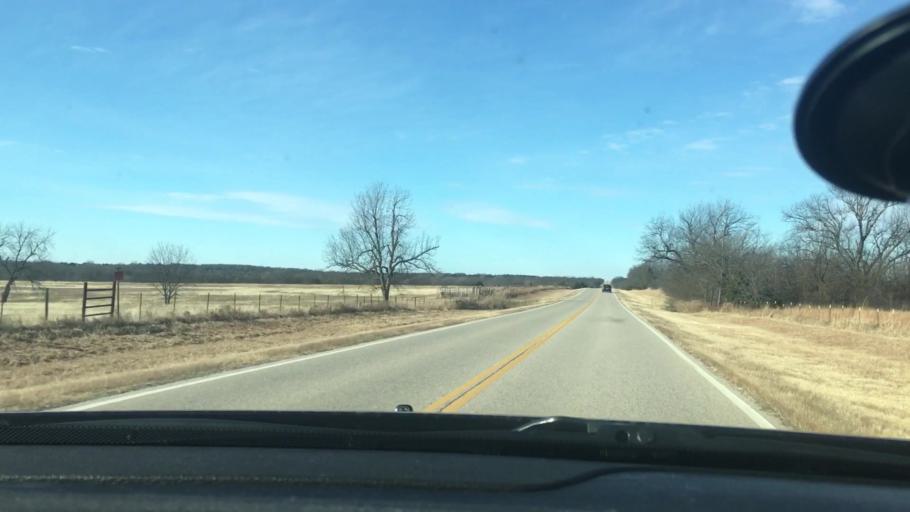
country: US
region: Oklahoma
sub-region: Garvin County
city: Stratford
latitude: 34.9860
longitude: -96.9952
